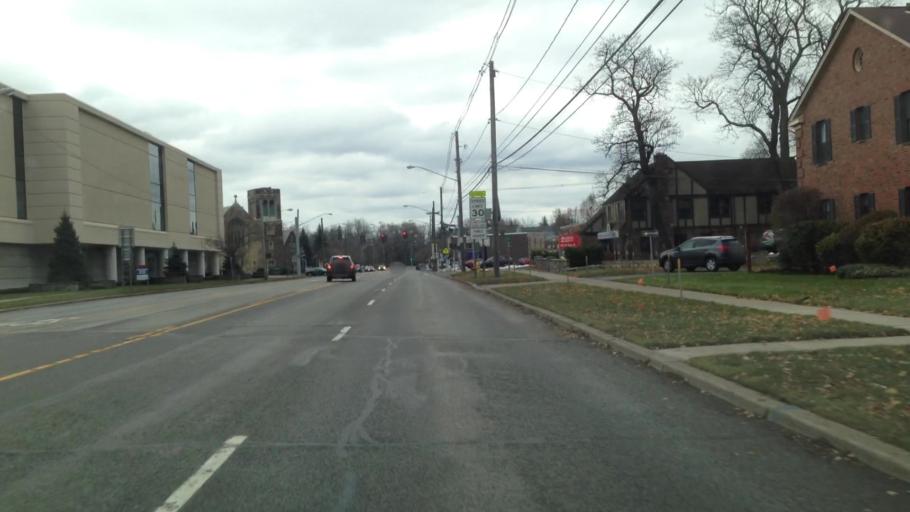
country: US
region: New York
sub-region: Erie County
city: Eggertsville
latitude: 42.9627
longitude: -78.8055
